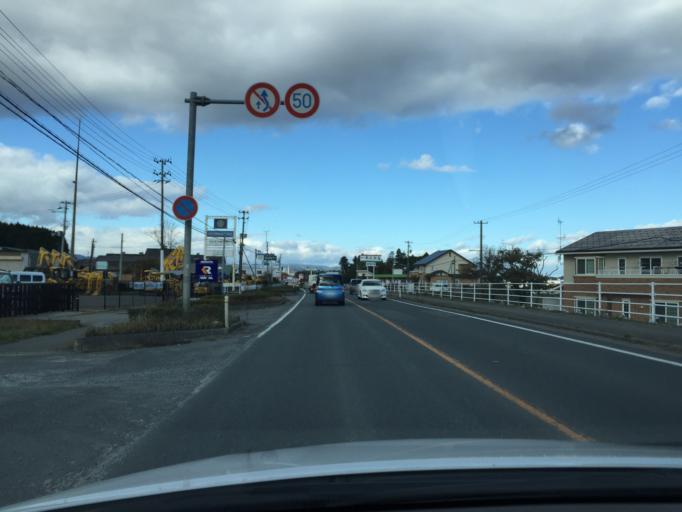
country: JP
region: Fukushima
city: Namie
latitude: 37.6213
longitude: 140.9969
